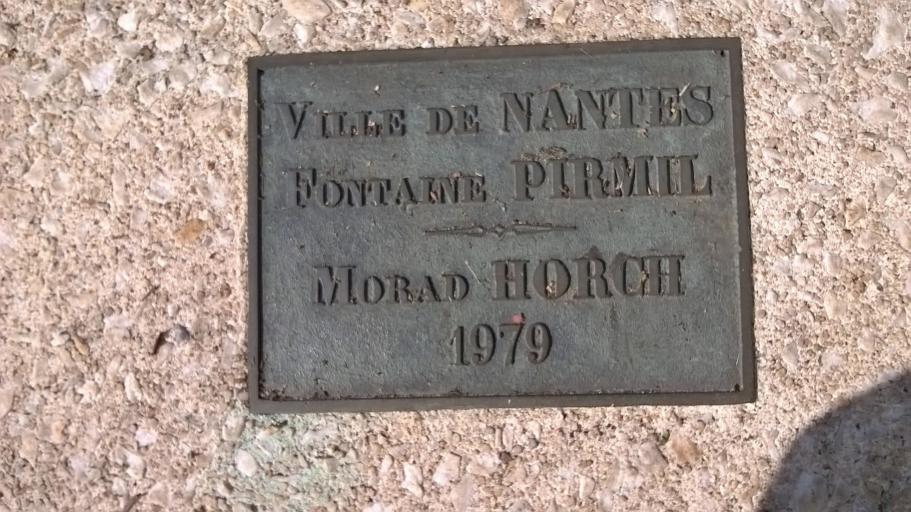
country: FR
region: Pays de la Loire
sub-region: Departement de la Loire-Atlantique
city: Reze
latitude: 47.1962
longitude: -1.5414
